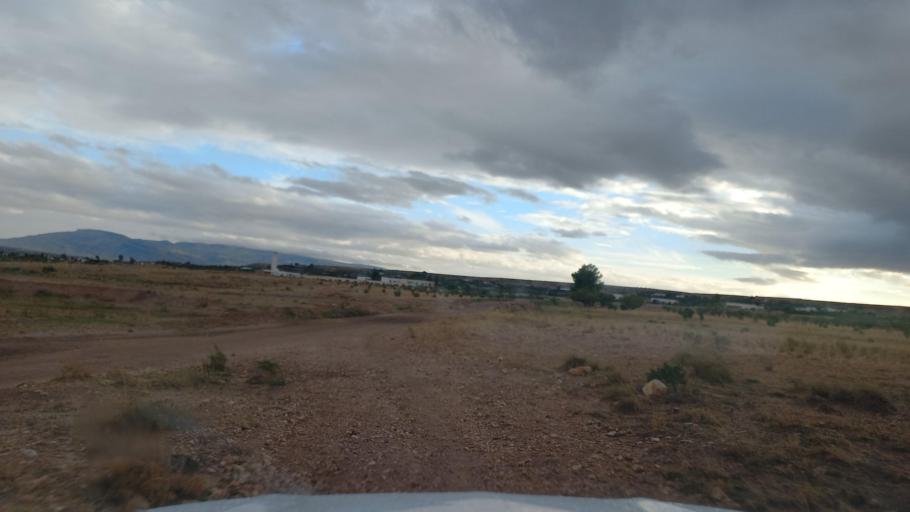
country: TN
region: Al Qasrayn
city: Kasserine
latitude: 35.2696
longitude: 8.9359
